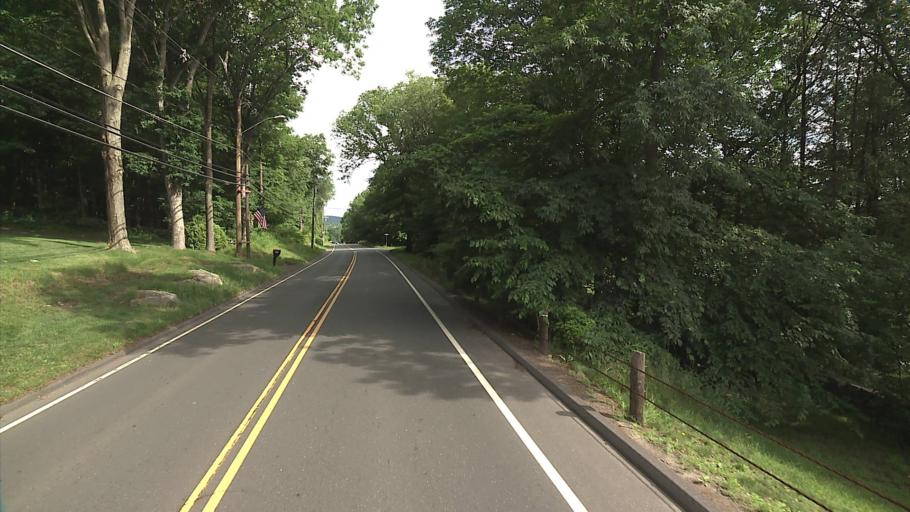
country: US
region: Connecticut
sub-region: Litchfield County
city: Oakville
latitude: 41.5854
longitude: -73.1027
